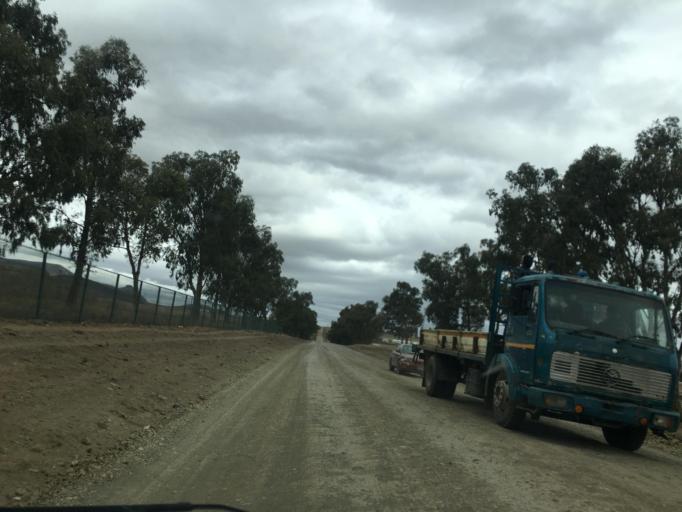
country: ZA
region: Eastern Cape
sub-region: Chris Hani District Municipality
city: Cala
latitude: -31.5362
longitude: 27.6886
